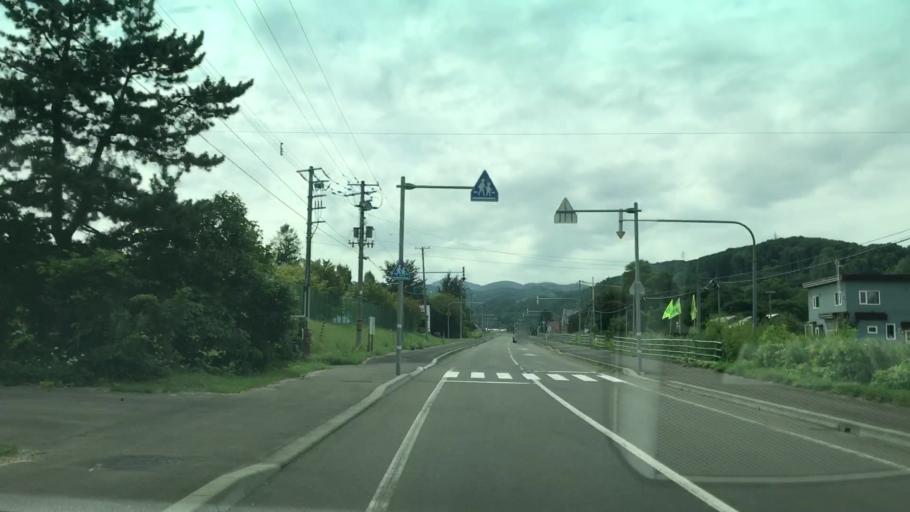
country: JP
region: Hokkaido
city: Yoichi
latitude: 43.1822
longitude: 140.8449
